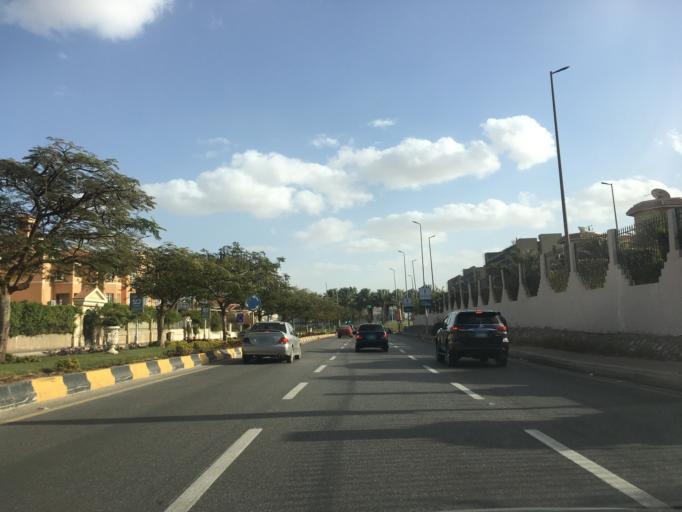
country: EG
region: Al Jizah
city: Awsim
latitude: 30.0238
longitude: 31.0036
